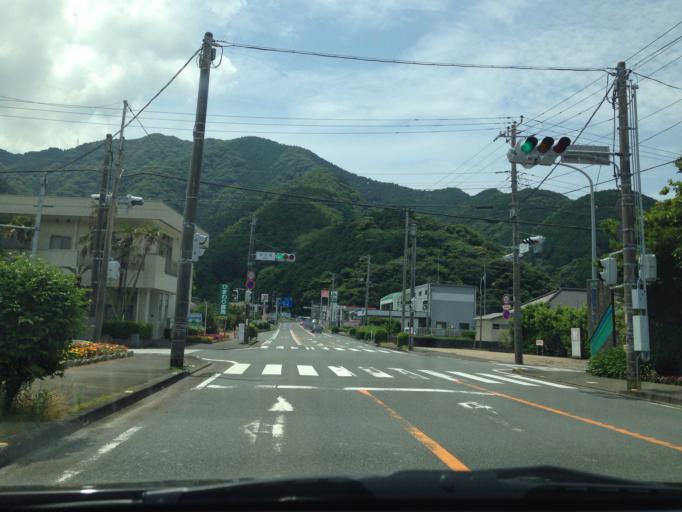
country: JP
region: Shizuoka
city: Heda
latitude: 34.8487
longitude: 138.7770
